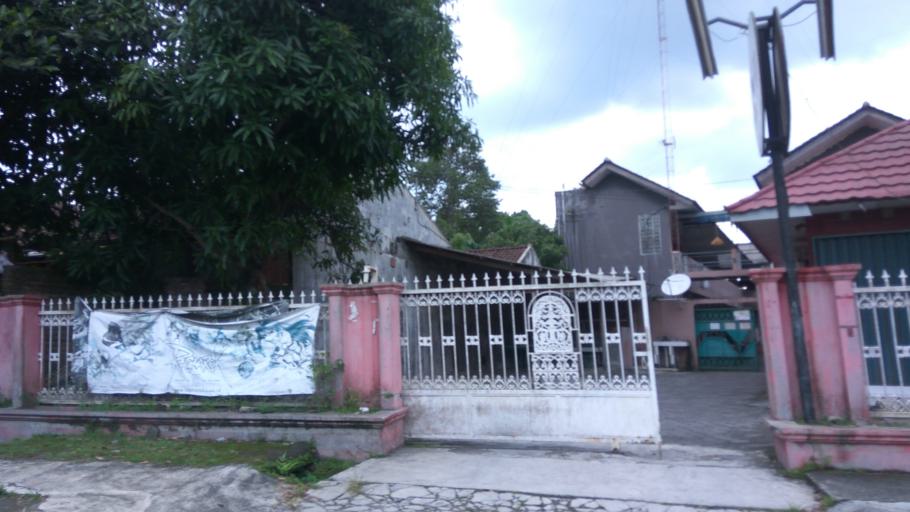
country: ID
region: Daerah Istimewa Yogyakarta
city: Melati
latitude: -7.7290
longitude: 110.4035
